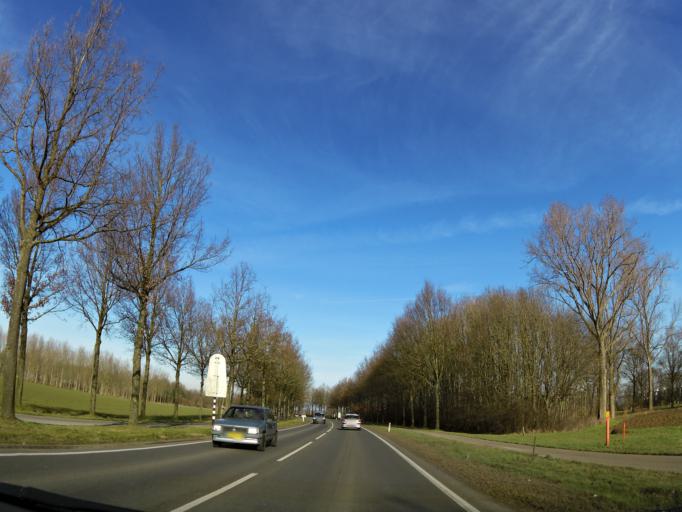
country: NL
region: Limburg
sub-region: Gemeente Sittard-Geleen
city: Limbricht
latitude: 51.0210
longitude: 5.8552
